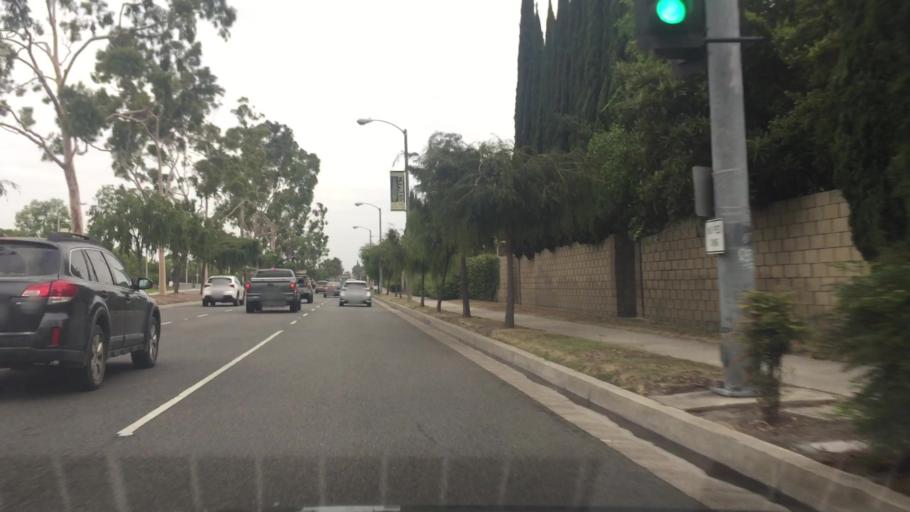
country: US
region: California
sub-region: Orange County
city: Cypress
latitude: 33.7978
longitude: -118.0282
